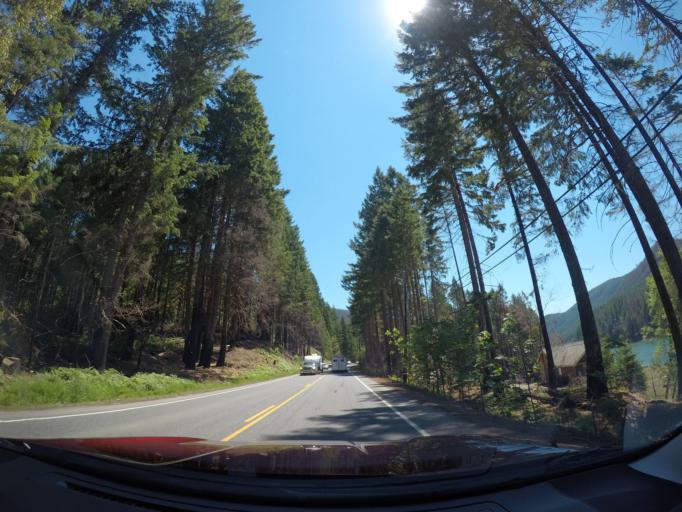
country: US
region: Oregon
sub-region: Linn County
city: Mill City
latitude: 44.7286
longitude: -122.1411
